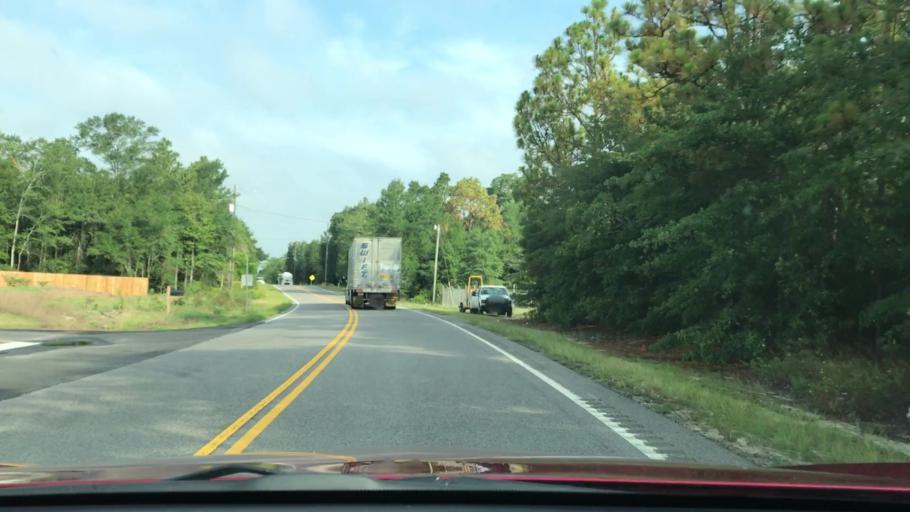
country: US
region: South Carolina
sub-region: Barnwell County
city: Williston
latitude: 33.6297
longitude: -81.3036
